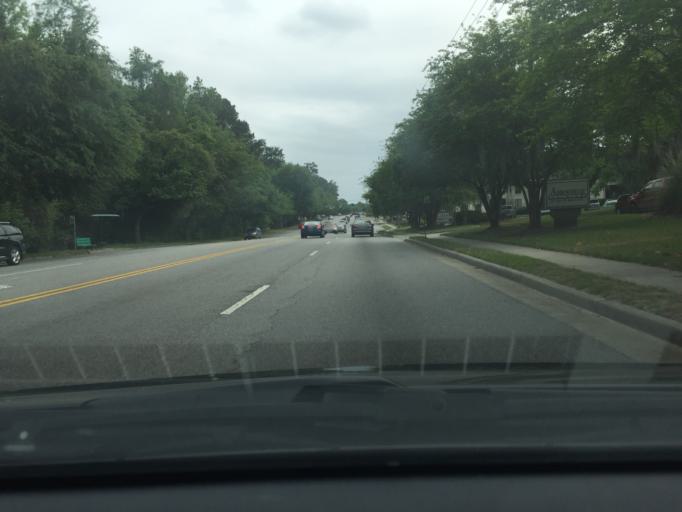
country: US
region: Georgia
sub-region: Chatham County
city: Isle of Hope
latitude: 32.0010
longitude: -81.1030
